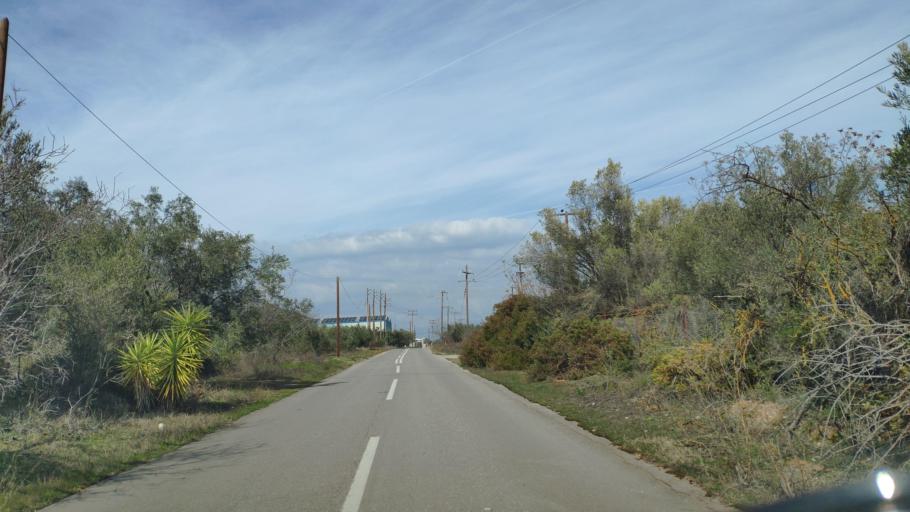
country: GR
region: Central Greece
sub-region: Nomos Evvoias
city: Vathi
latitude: 38.4257
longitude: 23.5911
